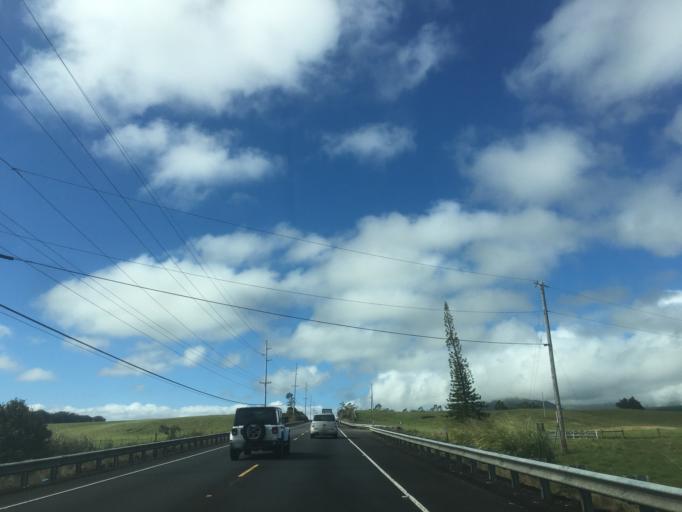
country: US
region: Hawaii
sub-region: Hawaii County
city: Waimea
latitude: 20.0483
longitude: -155.5766
